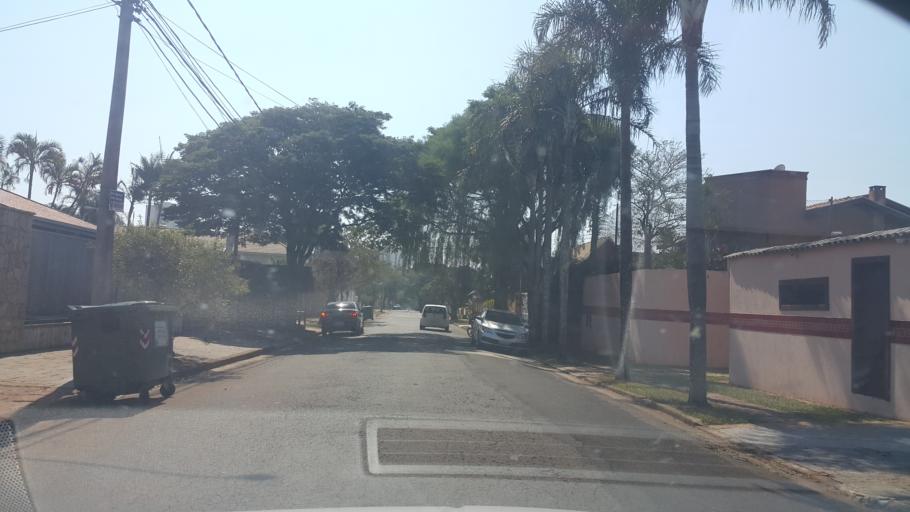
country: BR
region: Sao Paulo
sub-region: Campinas
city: Campinas
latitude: -22.8601
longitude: -47.0516
